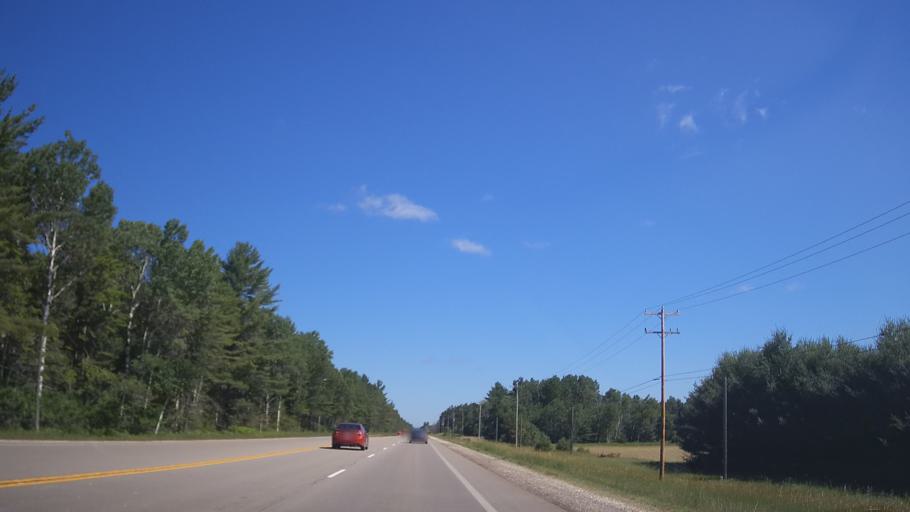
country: US
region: Michigan
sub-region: Cheboygan County
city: Indian River
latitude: 45.5124
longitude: -84.7814
